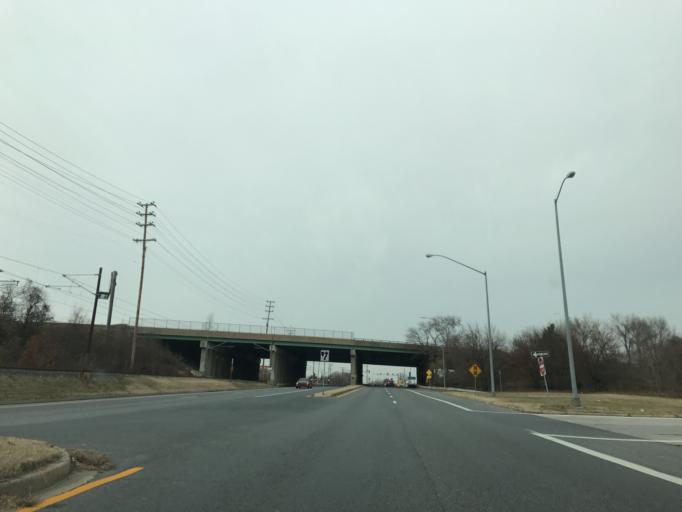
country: US
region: Maryland
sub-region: Anne Arundel County
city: Ferndale
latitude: 39.1752
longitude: -76.6353
